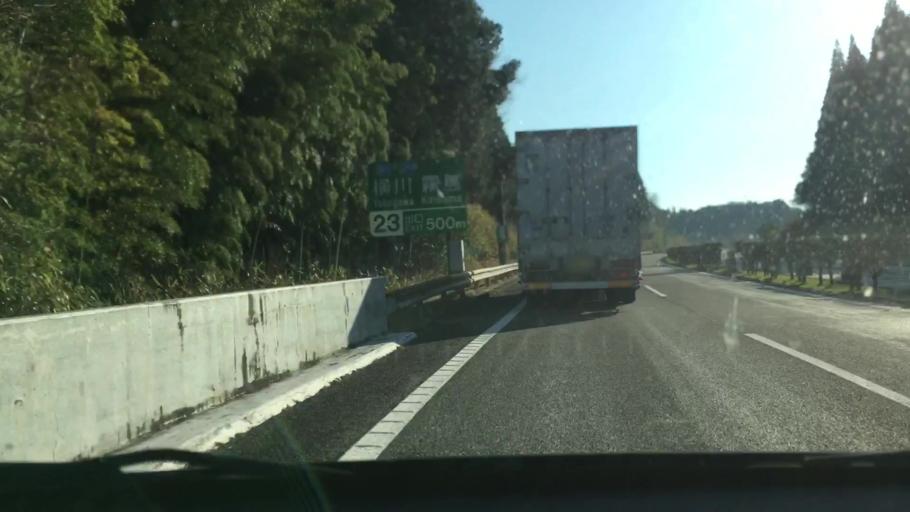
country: JP
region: Kagoshima
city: Kajiki
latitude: 31.9009
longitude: 130.7071
